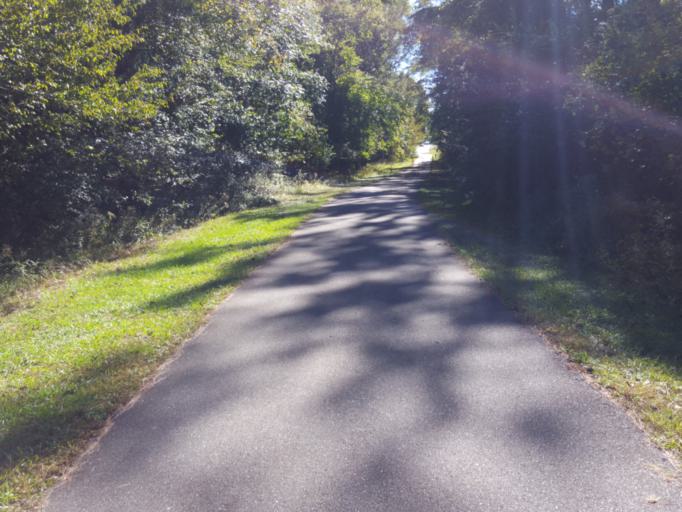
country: US
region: North Carolina
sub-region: Pitt County
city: Greenville
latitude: 35.6115
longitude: -77.3408
